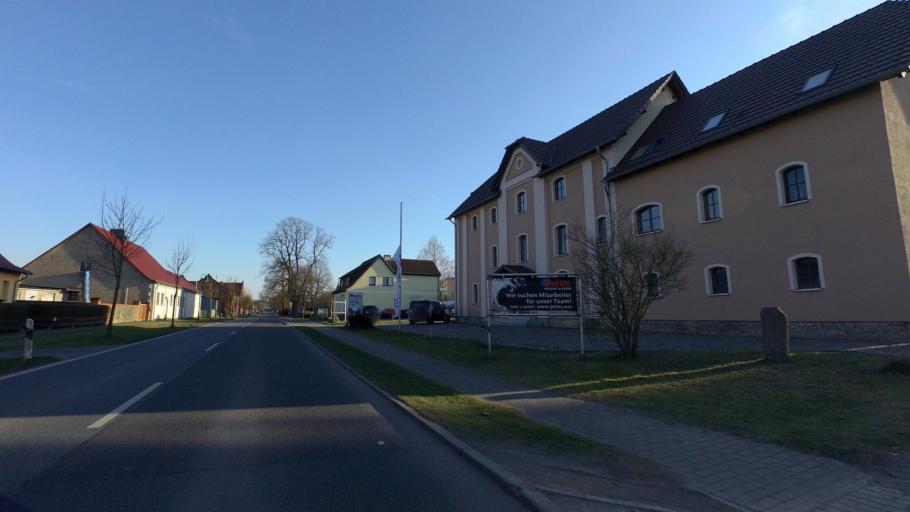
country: DE
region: Brandenburg
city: Eberswalde
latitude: 52.7781
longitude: 13.8361
